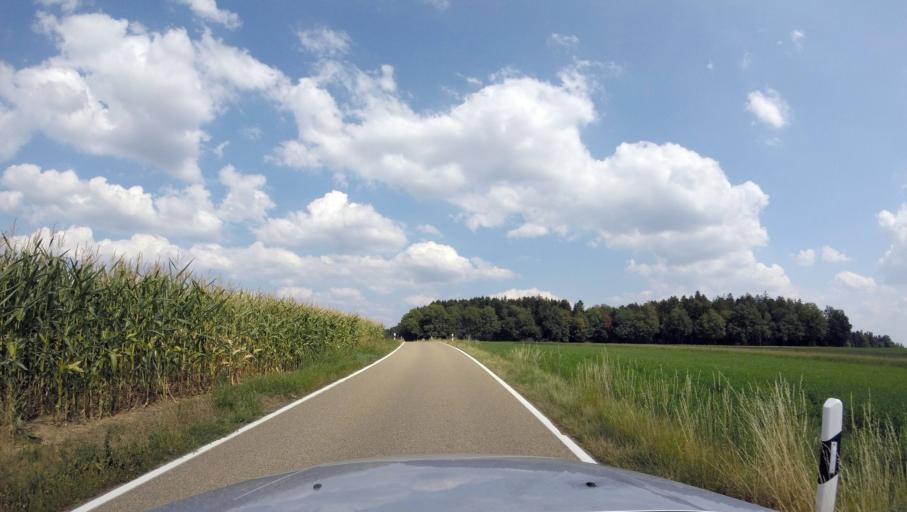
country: DE
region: Baden-Wuerttemberg
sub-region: Regierungsbezirk Stuttgart
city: Welzheim
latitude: 48.8754
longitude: 9.6793
